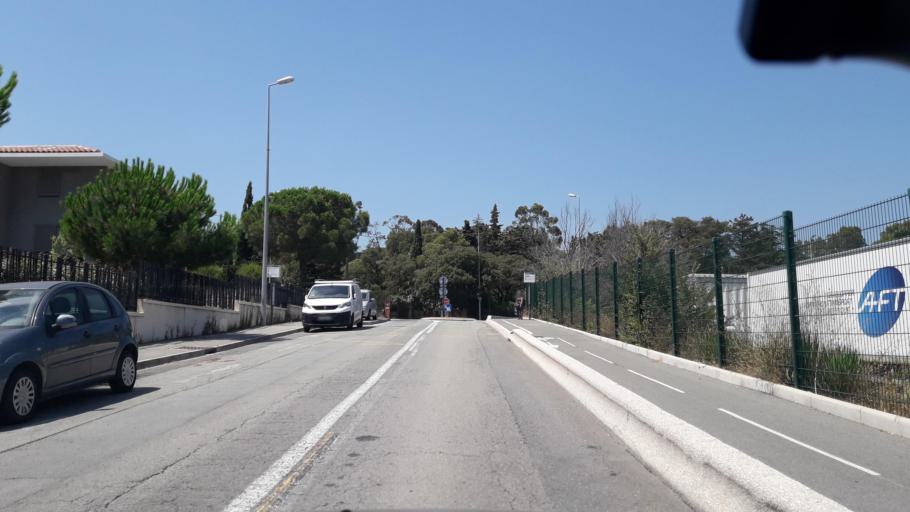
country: FR
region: Provence-Alpes-Cote d'Azur
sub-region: Departement du Var
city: Frejus
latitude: 43.4467
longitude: 6.7527
